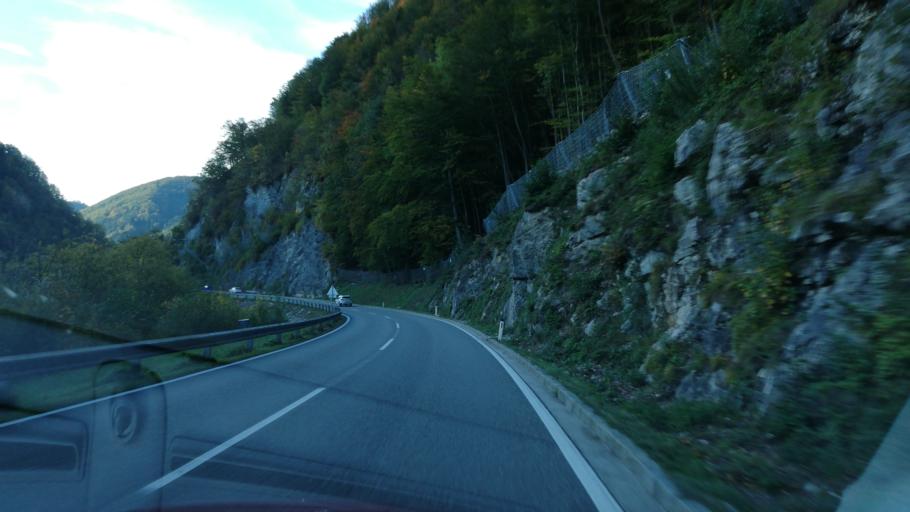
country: AT
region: Upper Austria
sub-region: Politischer Bezirk Steyr-Land
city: Weyer
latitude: 47.8706
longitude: 14.6094
